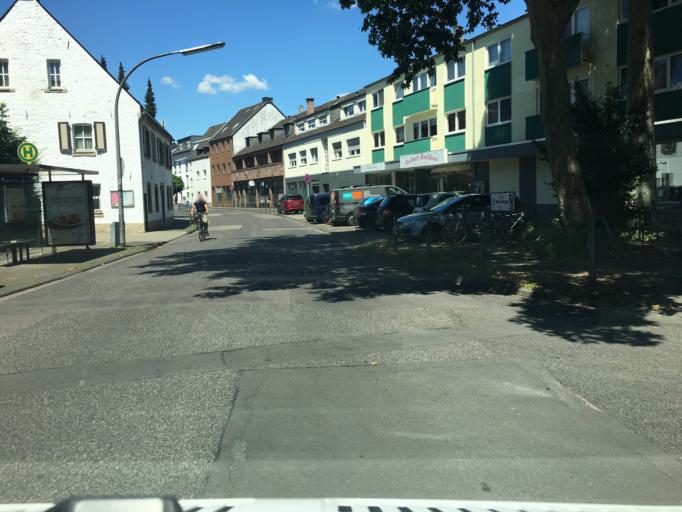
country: DE
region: North Rhine-Westphalia
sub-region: Regierungsbezirk Koln
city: Mengenich
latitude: 50.9729
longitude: 6.8659
